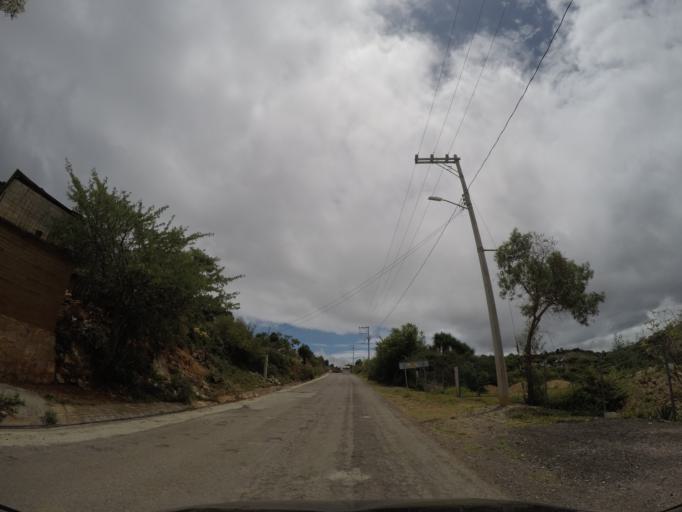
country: MX
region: Oaxaca
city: San Lorenzo Albarradas
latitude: 16.9172
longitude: -96.2573
